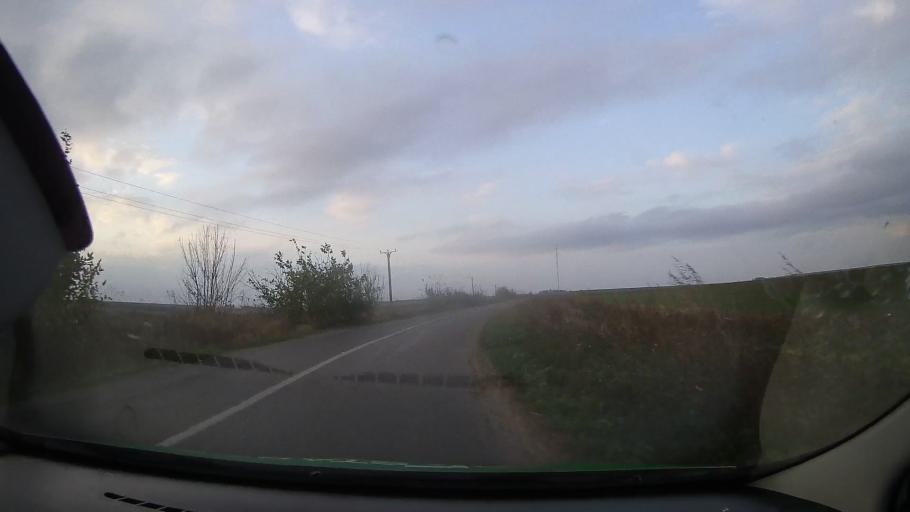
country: RO
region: Constanta
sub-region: Comuna Dobromir
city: Dobromir
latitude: 44.0359
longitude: 27.7596
